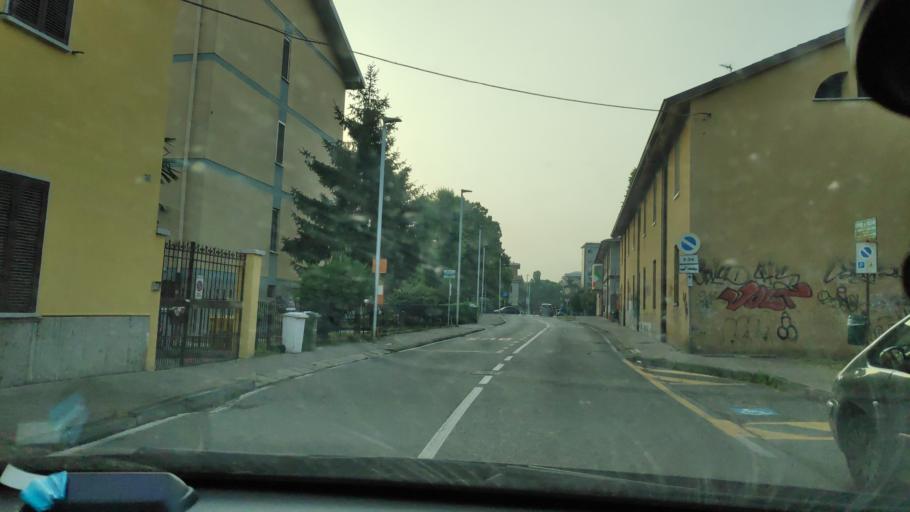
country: IT
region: Lombardy
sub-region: Citta metropolitana di Milano
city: Rozzano
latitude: 45.3753
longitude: 9.1462
